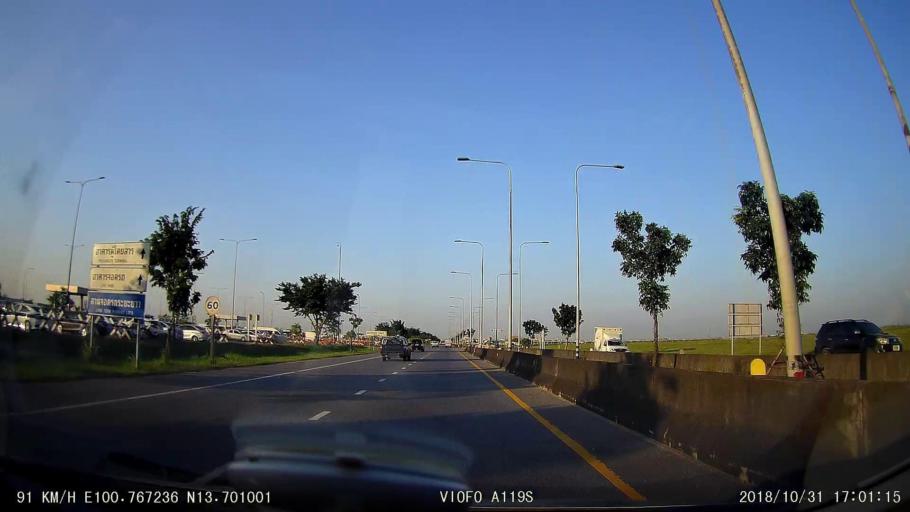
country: TH
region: Bangkok
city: Lat Krabang
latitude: 13.7013
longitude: 100.7673
